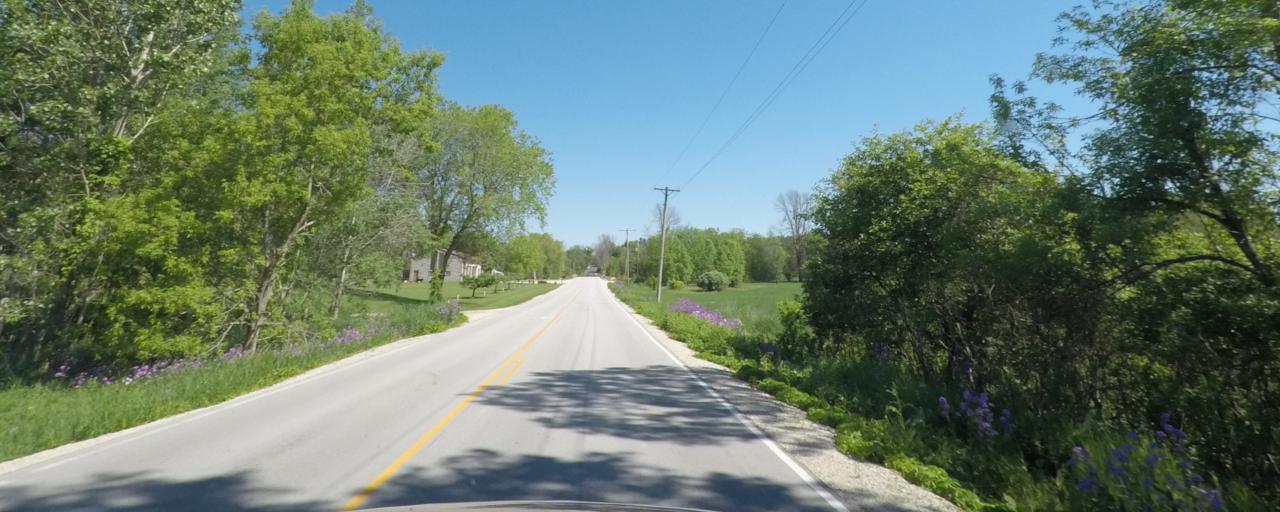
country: US
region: Wisconsin
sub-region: Sheboygan County
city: Sheboygan Falls
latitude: 43.7396
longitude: -87.8402
